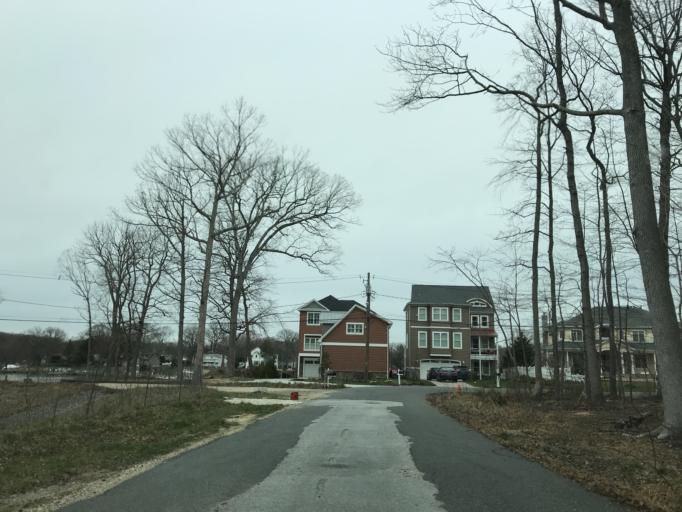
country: US
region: Maryland
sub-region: Baltimore County
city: Middle River
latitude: 39.3017
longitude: -76.4251
